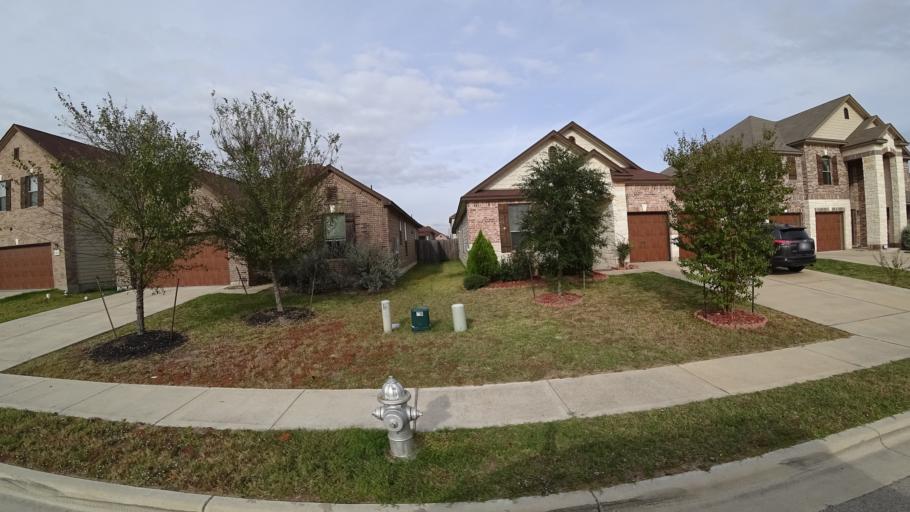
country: US
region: Texas
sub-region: Travis County
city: Wells Branch
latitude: 30.4314
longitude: -97.6616
